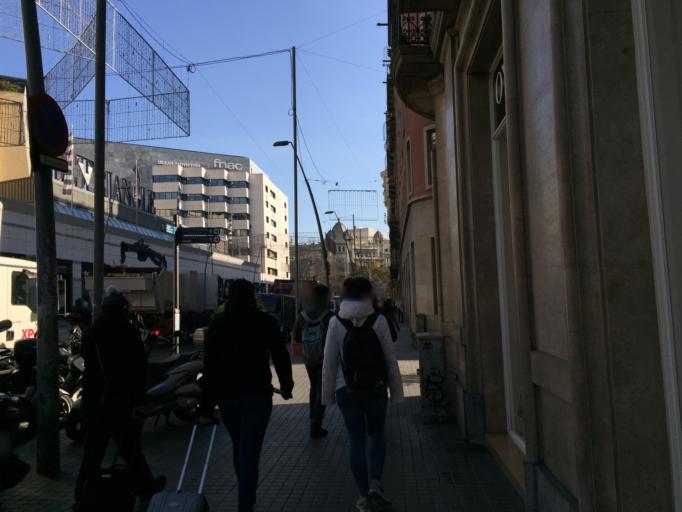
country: ES
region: Catalonia
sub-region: Provincia de Barcelona
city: Eixample
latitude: 41.3857
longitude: 2.1675
